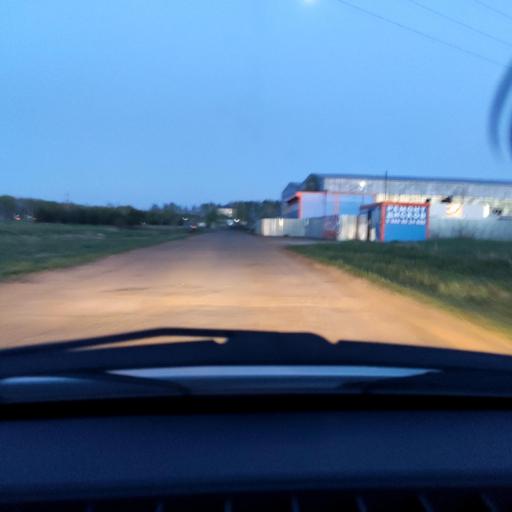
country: RU
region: Bashkortostan
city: Mikhaylovka
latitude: 54.8639
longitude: 55.7472
